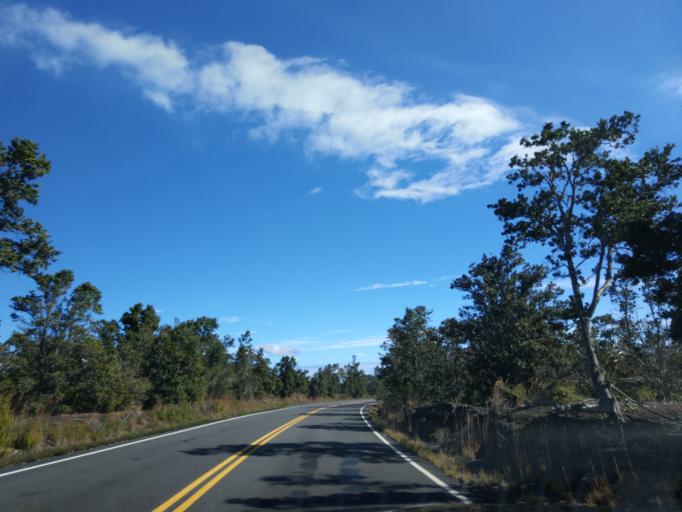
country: US
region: Hawaii
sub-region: Hawaii County
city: Volcano
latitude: 19.3461
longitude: -155.2134
